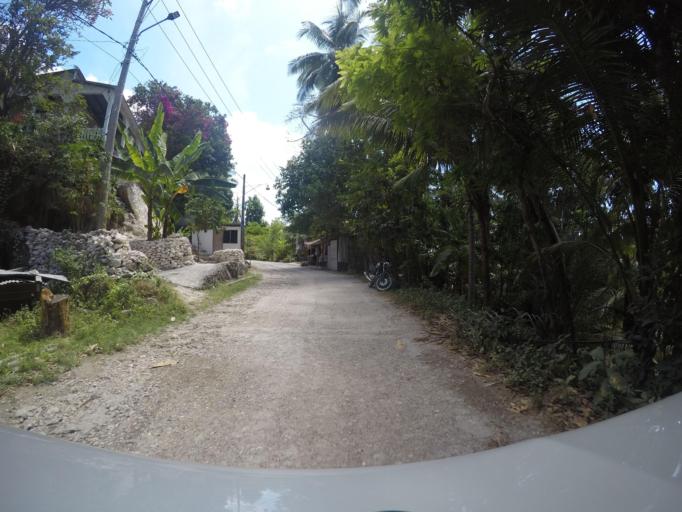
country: TL
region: Baucau
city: Baucau
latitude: -8.4581
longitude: 126.4490
